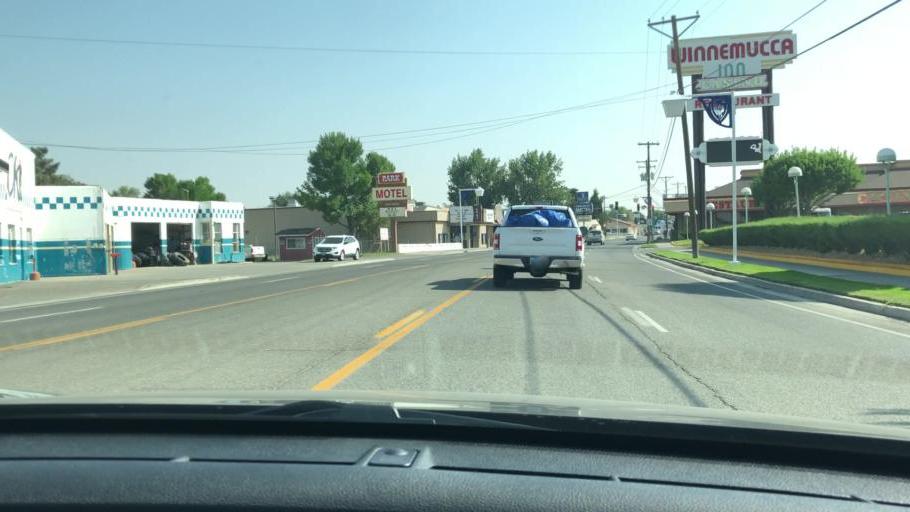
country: US
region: Nevada
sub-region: Humboldt County
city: Winnemucca
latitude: 40.9672
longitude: -117.7422
